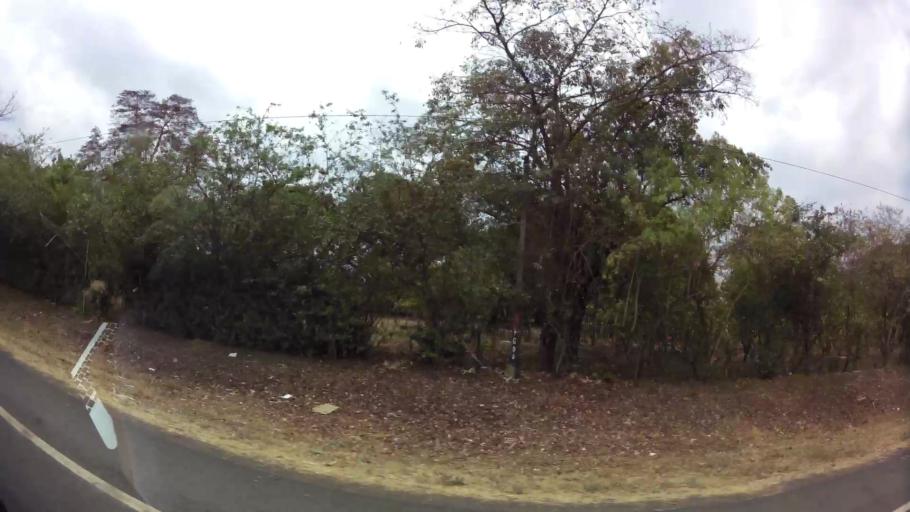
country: NI
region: Leon
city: Telica
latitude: 12.5212
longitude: -86.8684
